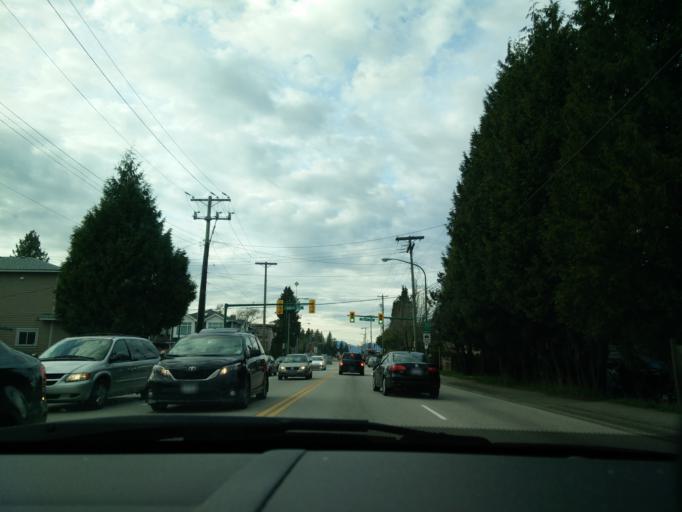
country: CA
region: British Columbia
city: New Westminster
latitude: 49.2224
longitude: -122.9387
